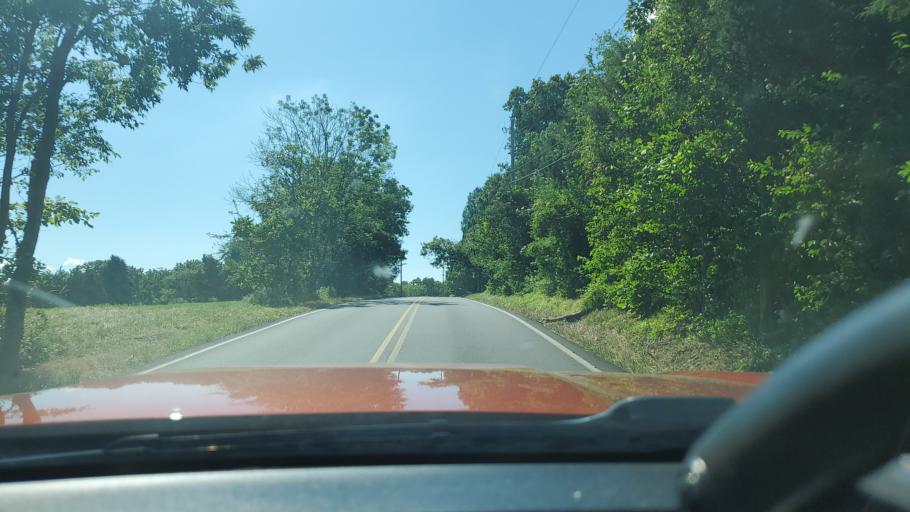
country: US
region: Pennsylvania
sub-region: Montgomery County
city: Red Hill
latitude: 40.3547
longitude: -75.5285
